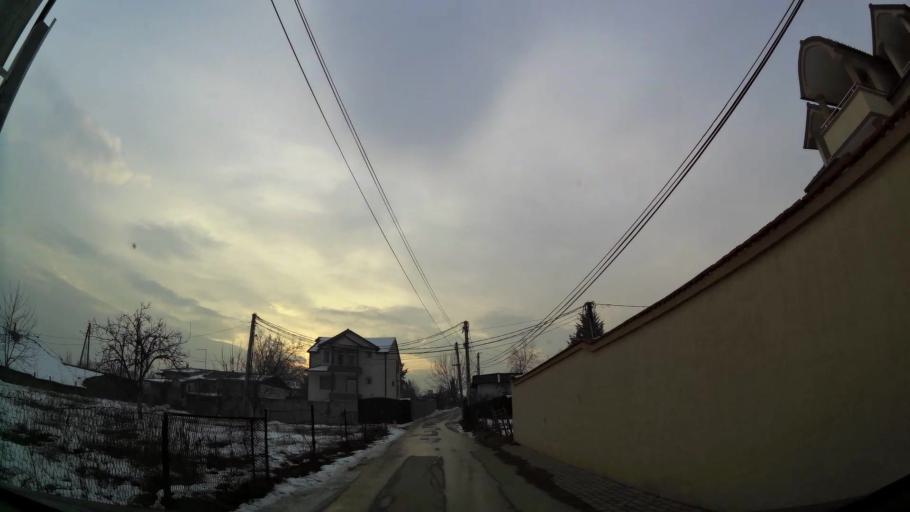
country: MK
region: Suto Orizari
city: Suto Orizare
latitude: 42.0308
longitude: 21.4231
